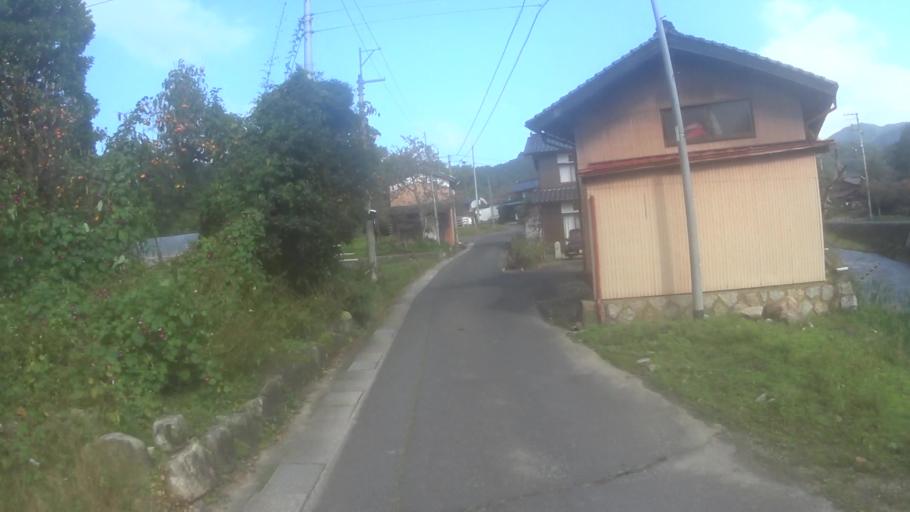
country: JP
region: Kyoto
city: Miyazu
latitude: 35.6077
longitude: 135.1478
